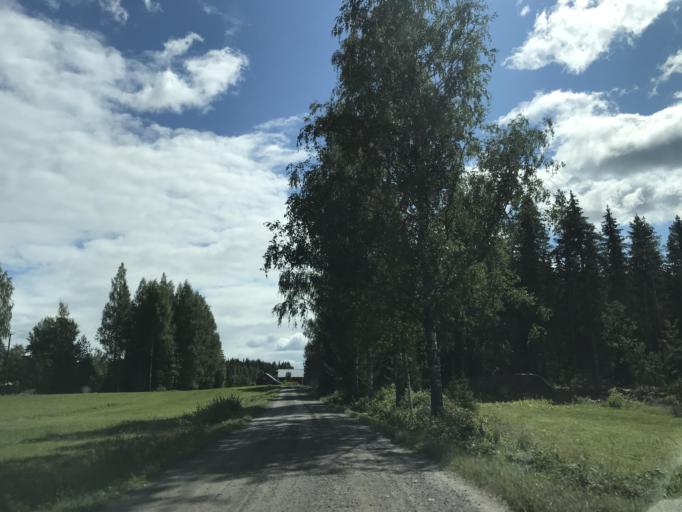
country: FI
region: Uusimaa
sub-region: Helsinki
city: Kaerkoelae
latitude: 60.6324
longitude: 23.8369
